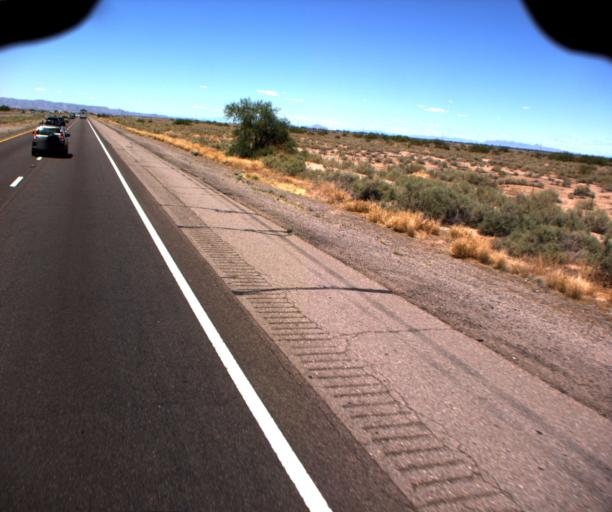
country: US
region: Arizona
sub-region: Pinal County
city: Casa Blanca
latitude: 33.1551
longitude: -111.8705
